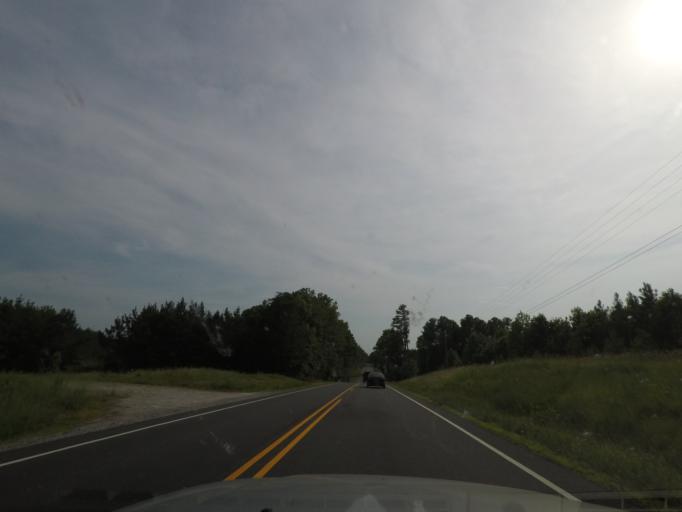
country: US
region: Virginia
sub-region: Prince Edward County
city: Hampden Sydney
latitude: 37.1180
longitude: -78.4590
